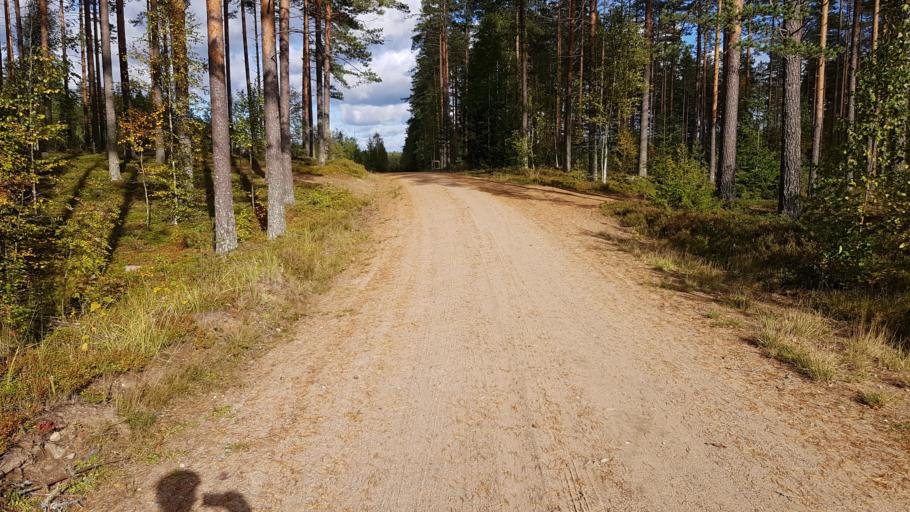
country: FI
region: South Karelia
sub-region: Imatra
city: Ruokolahti
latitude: 61.2536
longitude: 29.1010
